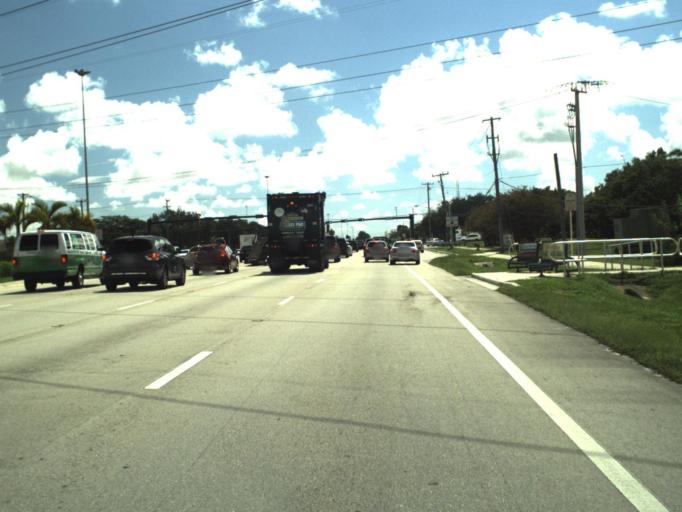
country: US
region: Florida
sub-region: Broward County
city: Cooper City
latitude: 26.0080
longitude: -80.2817
